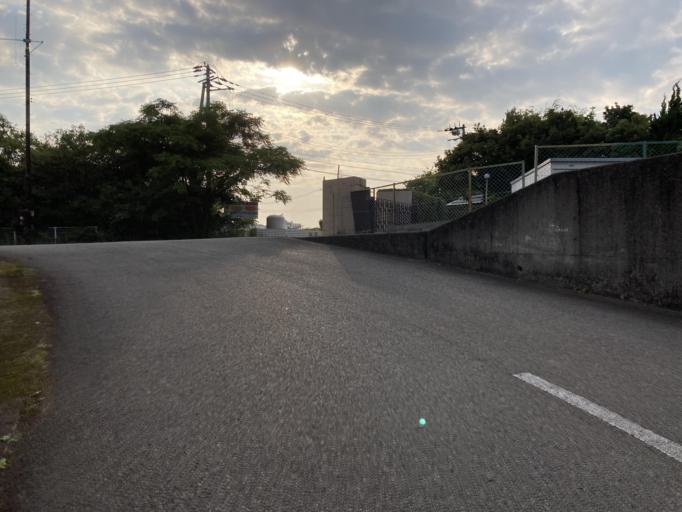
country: JP
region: Wakayama
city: Tanabe
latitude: 33.6835
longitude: 135.3580
